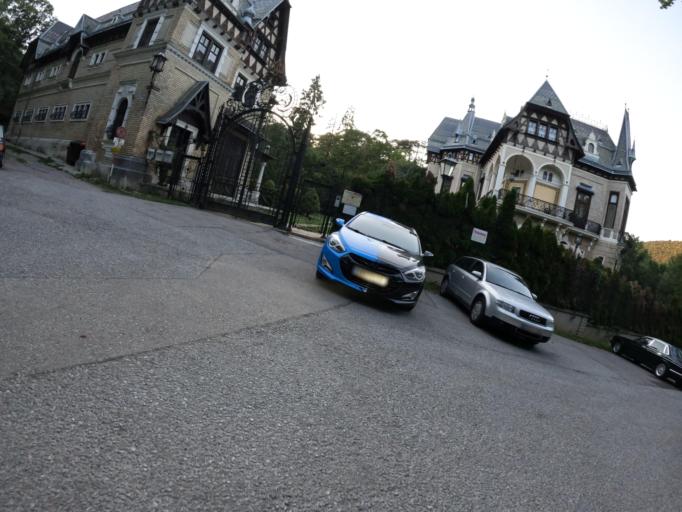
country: AT
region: Lower Austria
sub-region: Politischer Bezirk Baden
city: Baden
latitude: 48.0086
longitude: 16.2052
